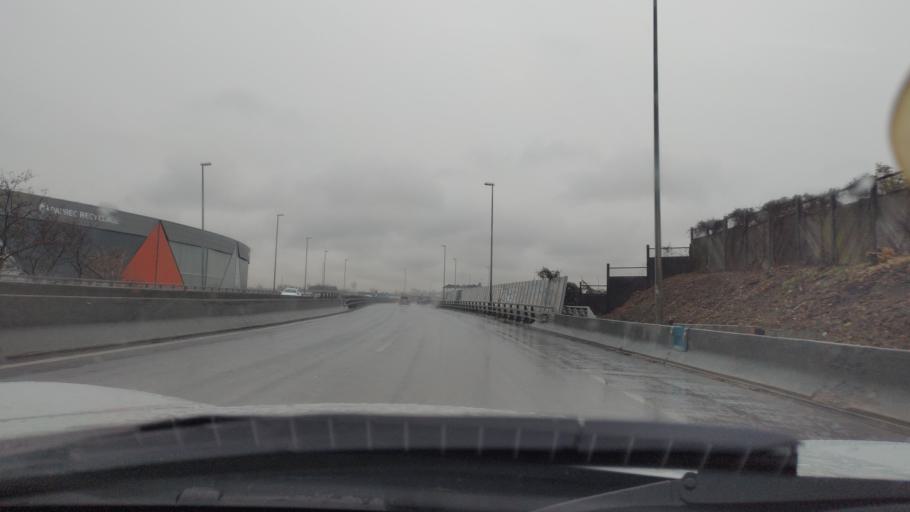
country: FR
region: Ile-de-France
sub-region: Departement de Seine-Saint-Denis
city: La Courneuve
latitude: 48.9291
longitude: 2.4029
